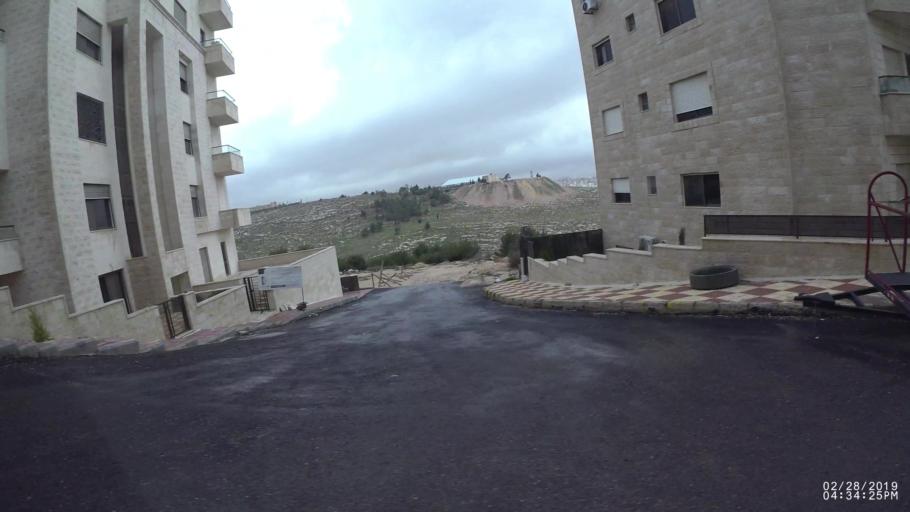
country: JO
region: Amman
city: Amman
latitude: 32.0083
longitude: 35.9318
